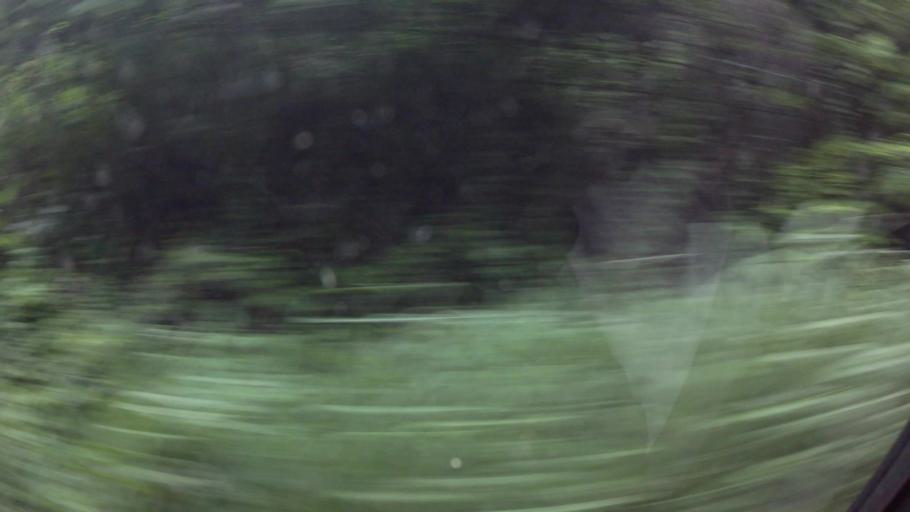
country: TH
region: Chon Buri
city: Sattahip
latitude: 12.6895
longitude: 100.9265
